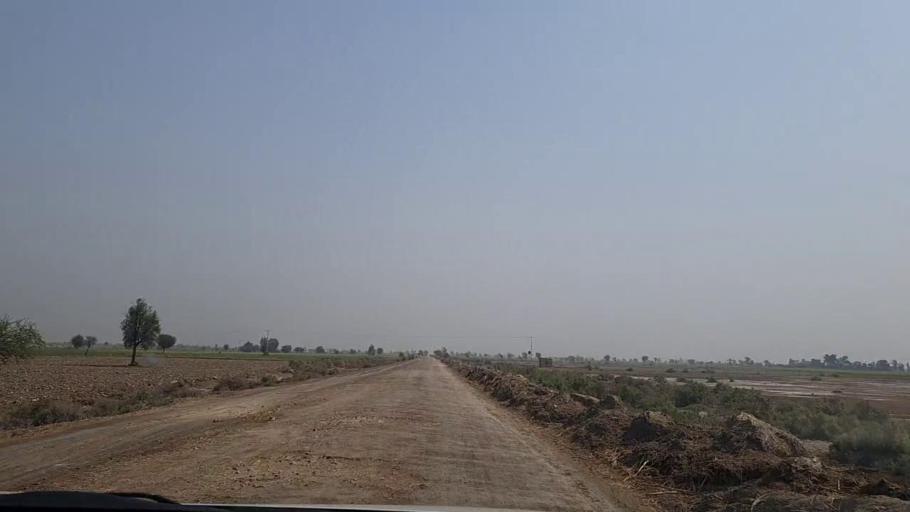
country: PK
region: Sindh
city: Mirpur Khas
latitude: 25.5570
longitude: 69.1986
